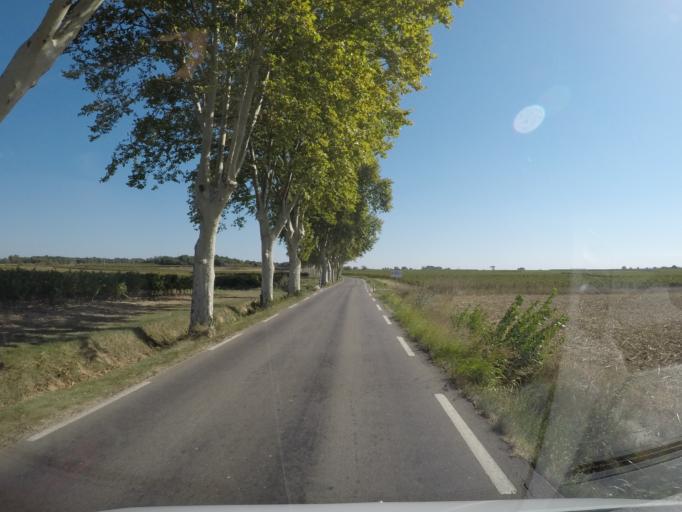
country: FR
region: Languedoc-Roussillon
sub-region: Departement du Gard
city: Saint-Chaptes
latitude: 43.9839
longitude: 4.2661
